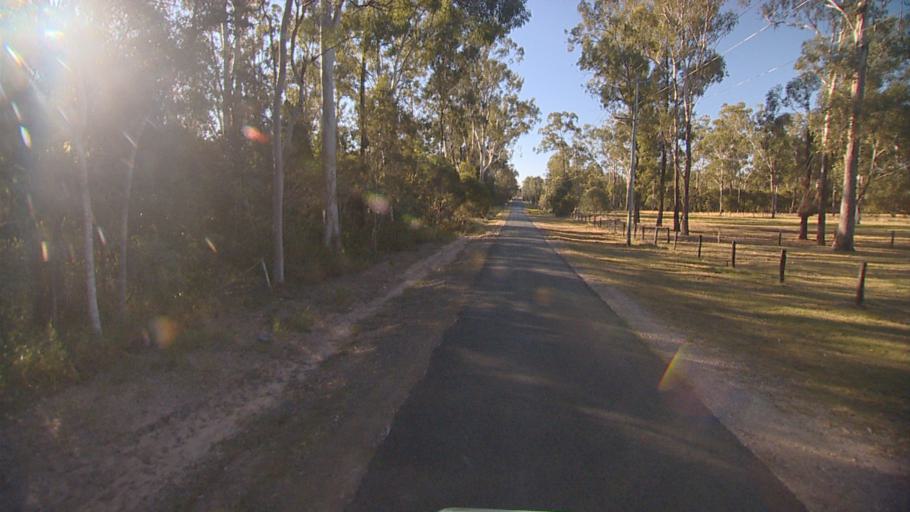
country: AU
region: Queensland
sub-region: Logan
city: North Maclean
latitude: -27.7851
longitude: 153.0457
